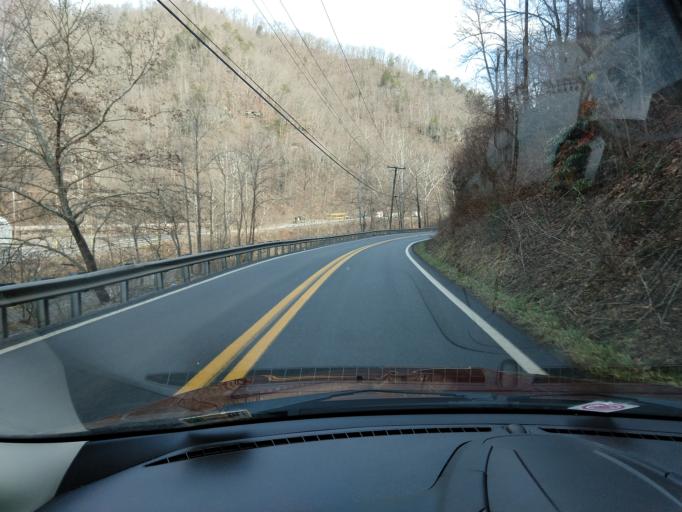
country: US
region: West Virginia
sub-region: McDowell County
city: Welch
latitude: 37.3448
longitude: -81.7427
